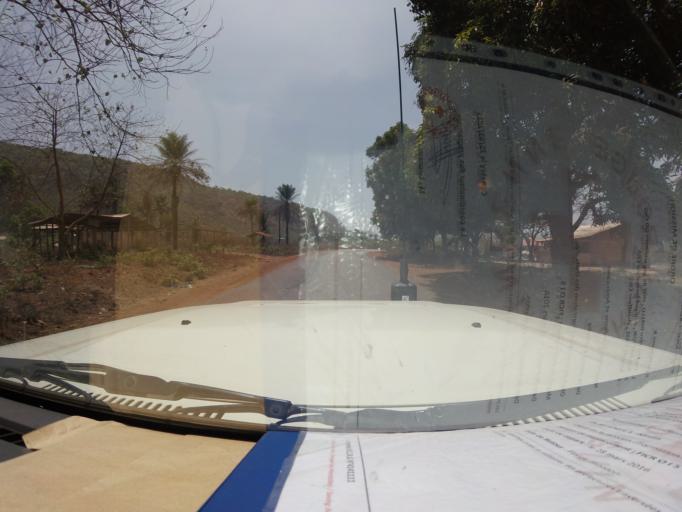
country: GN
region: Kindia
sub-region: Coyah
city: Coyah
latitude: 9.7835
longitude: -13.3226
